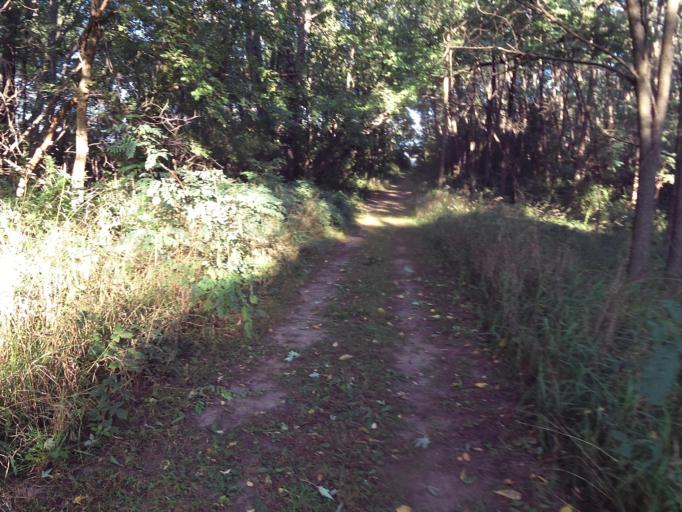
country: US
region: Minnesota
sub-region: Washington County
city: Lake Saint Croix Beach
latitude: 44.9341
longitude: -92.7934
